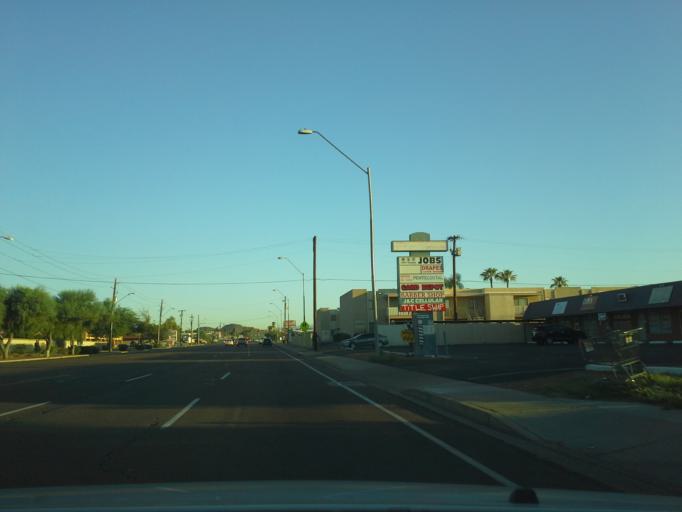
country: US
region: Arizona
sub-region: Maricopa County
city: Paradise Valley
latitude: 33.6371
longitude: -112.0307
